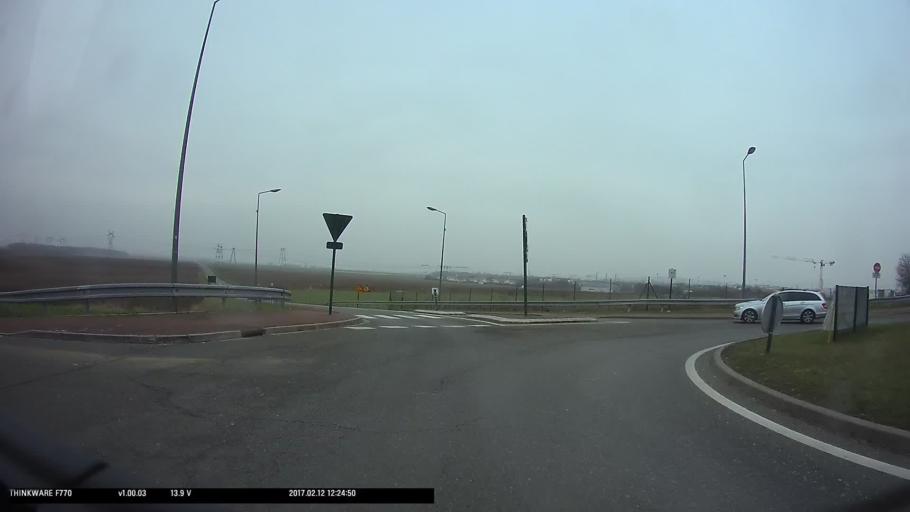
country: FR
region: Ile-de-France
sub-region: Departement du Val-d'Oise
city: Courdimanche
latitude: 49.0381
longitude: 1.9955
